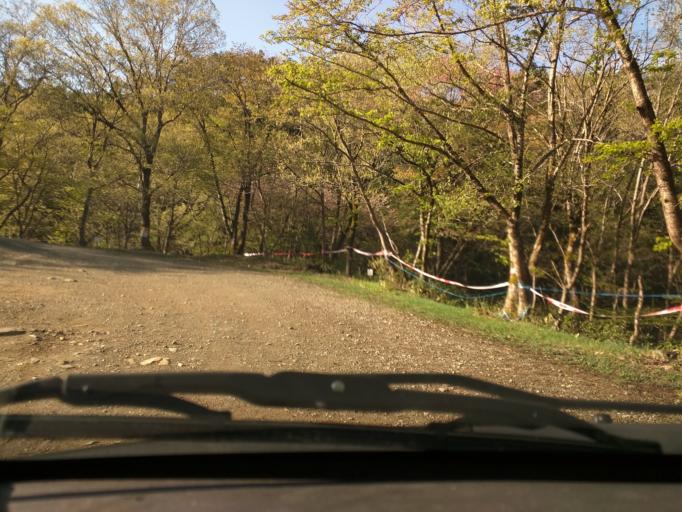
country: JP
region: Fukushima
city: Inawashiro
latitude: 37.5048
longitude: 139.9617
